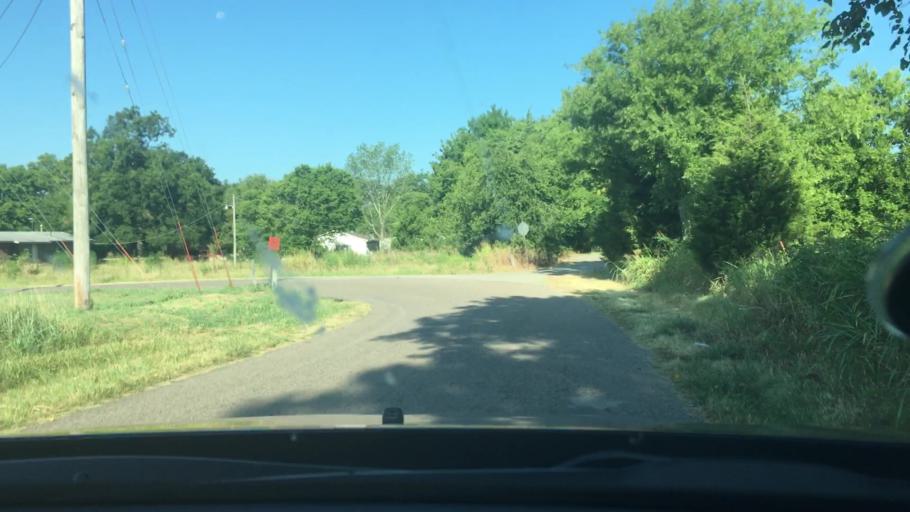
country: US
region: Oklahoma
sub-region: Murray County
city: Sulphur
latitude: 34.4049
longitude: -96.8194
